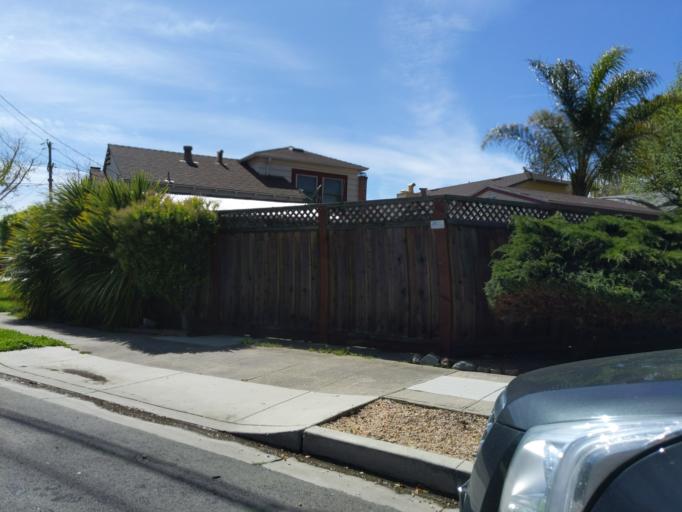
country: US
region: California
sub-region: Alameda County
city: Alameda
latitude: 37.7590
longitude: -122.2259
